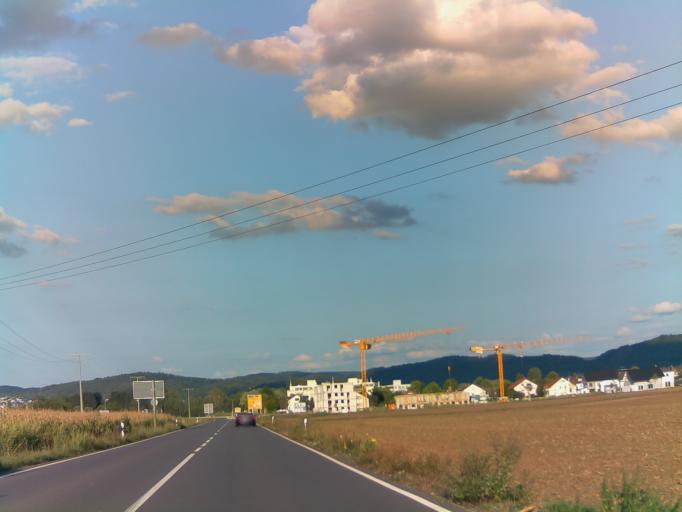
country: DE
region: Baden-Wuerttemberg
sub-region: Karlsruhe Region
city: Heddesheim
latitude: 49.5133
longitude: 8.5965
